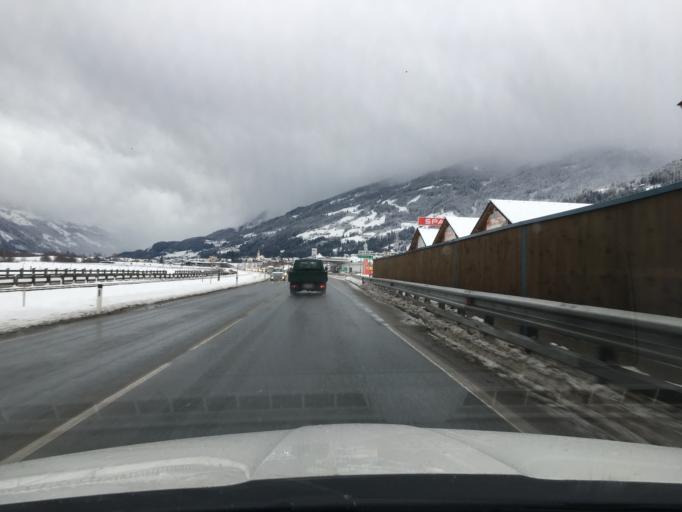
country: AT
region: Tyrol
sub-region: Politischer Bezirk Schwaz
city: Uderns
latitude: 47.3191
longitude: 11.8652
